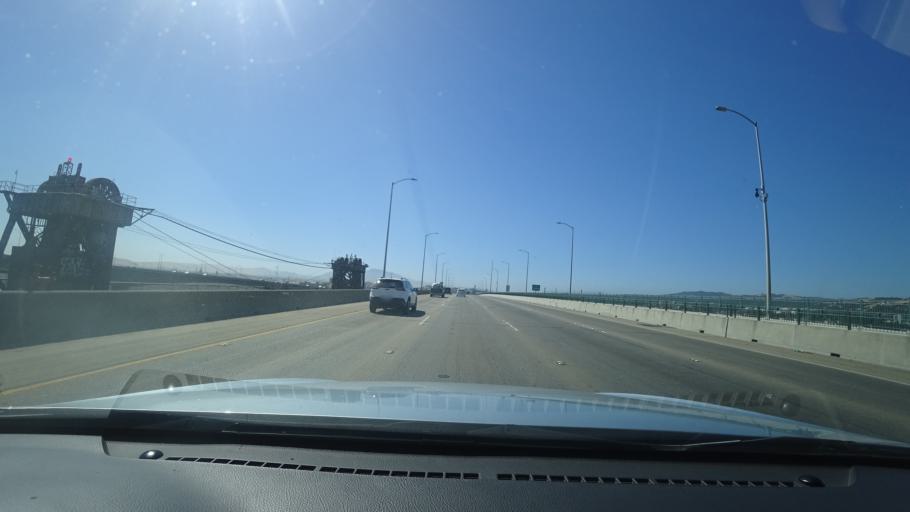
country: US
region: California
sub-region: Contra Costa County
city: Martinez
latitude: 38.0393
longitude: -122.1220
